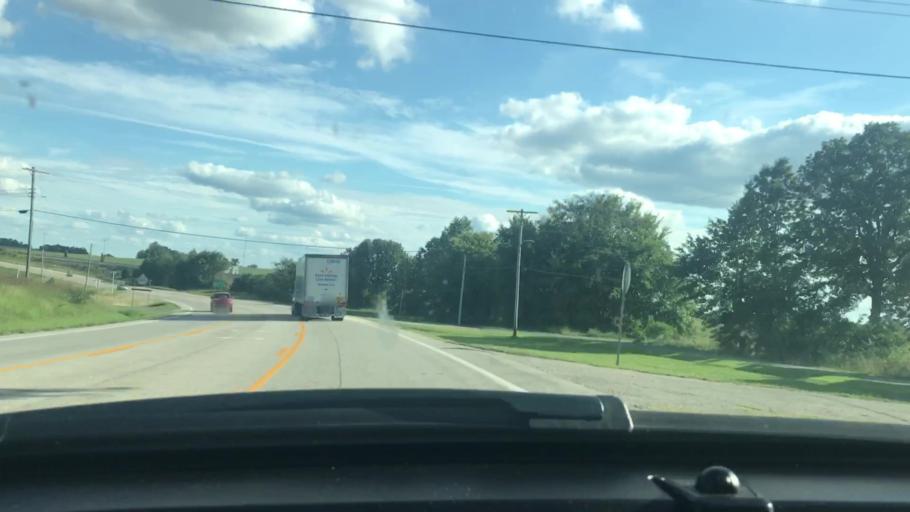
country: US
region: Missouri
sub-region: Oregon County
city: Thayer
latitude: 36.5934
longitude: -91.6439
